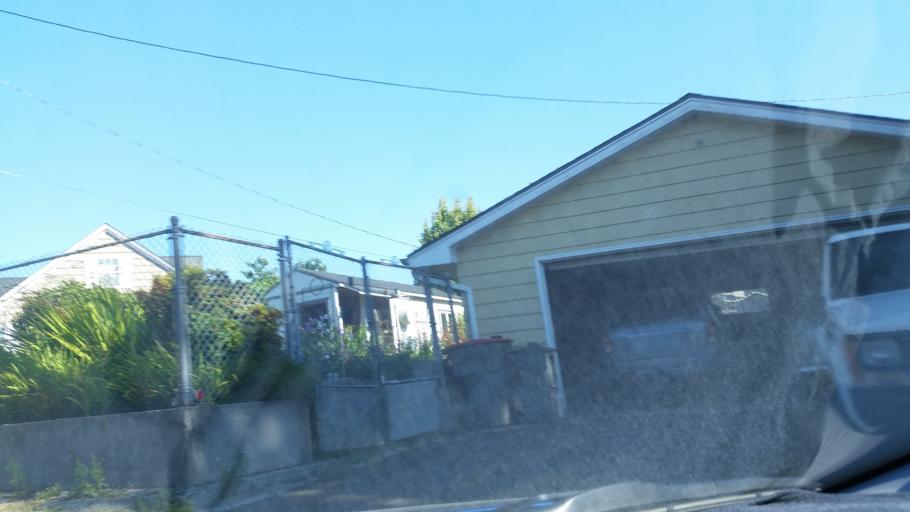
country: US
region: Oregon
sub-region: Clatsop County
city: Astoria
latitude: 46.1834
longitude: -123.8537
